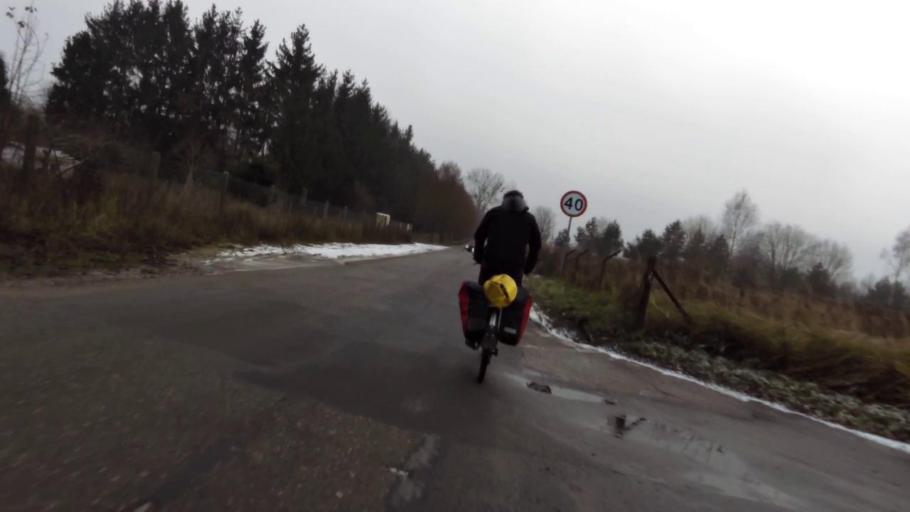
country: PL
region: West Pomeranian Voivodeship
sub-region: Powiat walecki
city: Walcz
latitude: 53.2866
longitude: 16.4738
